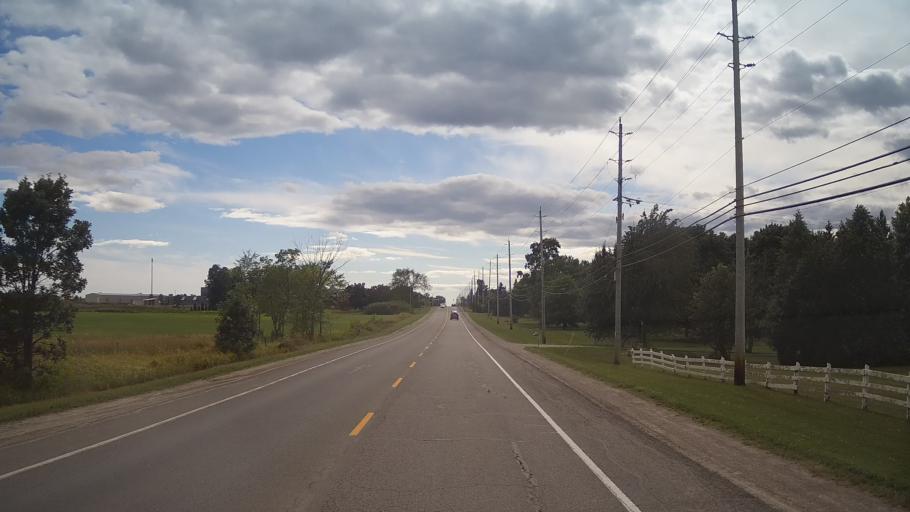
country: CA
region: Ontario
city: Kingston
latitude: 44.2795
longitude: -76.4396
